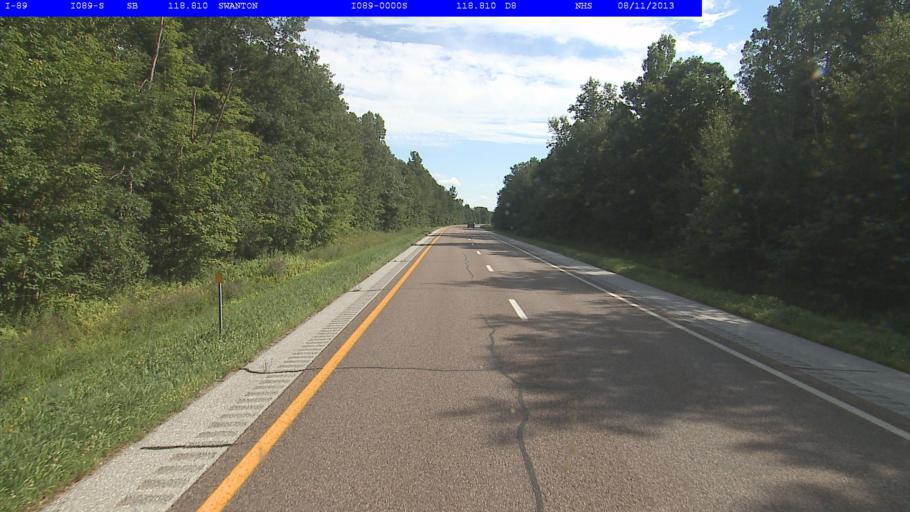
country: US
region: Vermont
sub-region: Franklin County
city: Saint Albans
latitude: 44.8597
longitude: -73.0824
